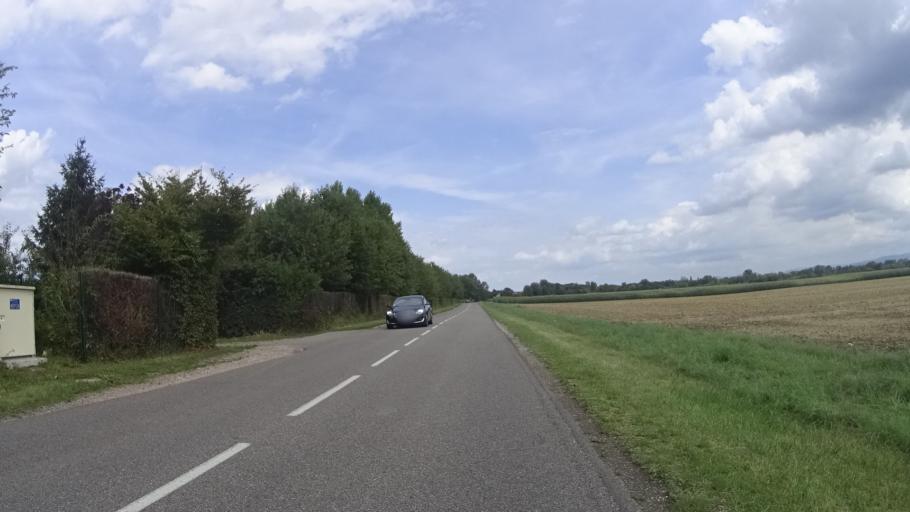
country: FR
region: Alsace
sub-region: Departement du Bas-Rhin
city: Gambsheim
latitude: 48.7030
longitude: 7.9031
